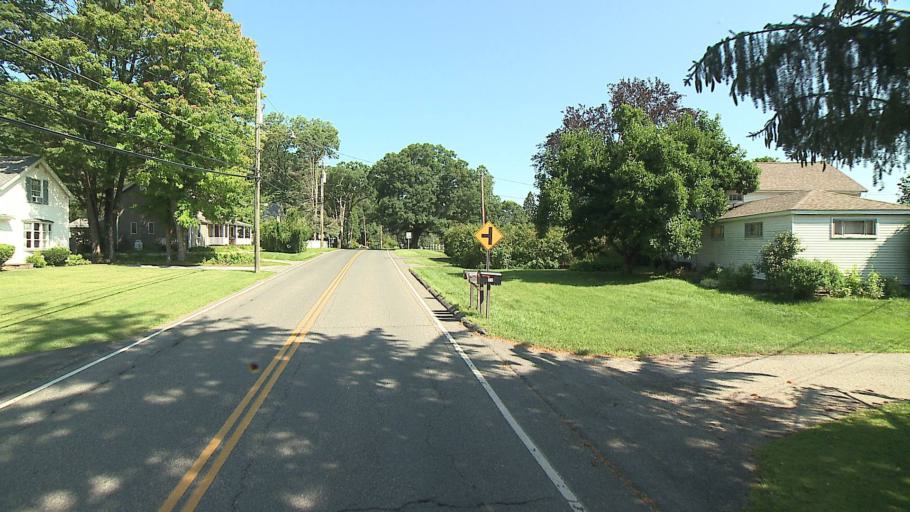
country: US
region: Connecticut
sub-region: Litchfield County
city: Canaan
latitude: 41.9863
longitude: -73.4233
